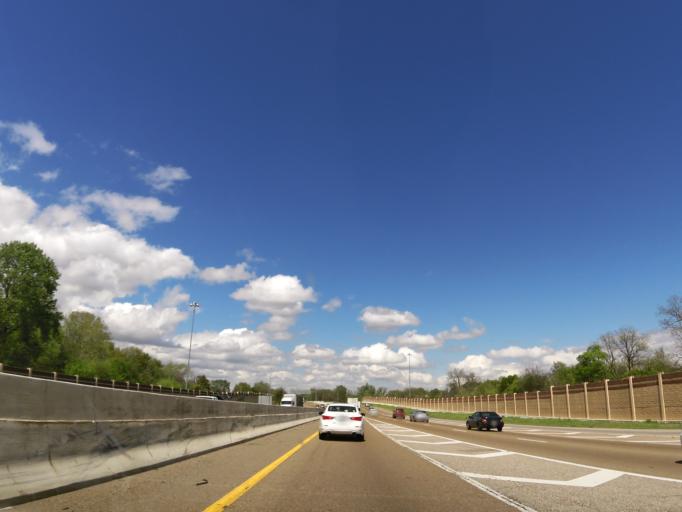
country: US
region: Tennessee
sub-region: Shelby County
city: Memphis
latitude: 35.1616
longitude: -90.0195
